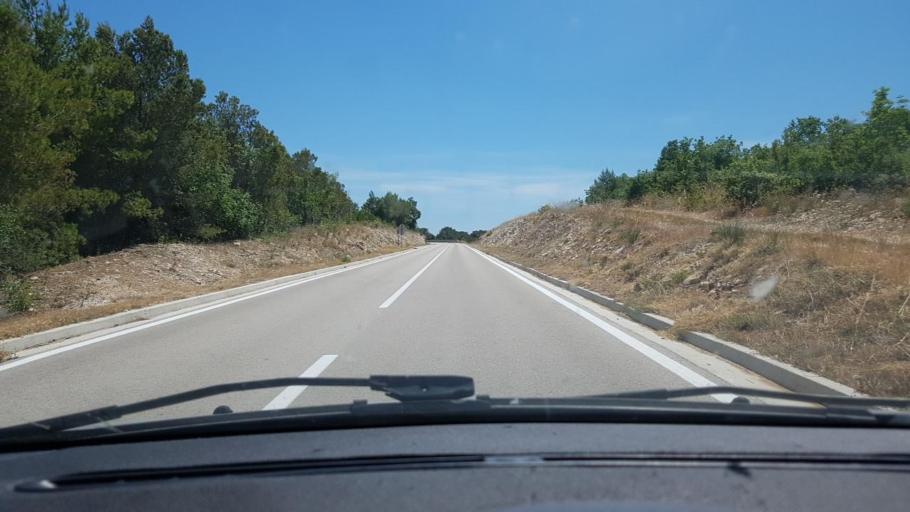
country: HR
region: Sibensko-Kniniska
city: Zaton
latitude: 43.8604
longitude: 15.9115
